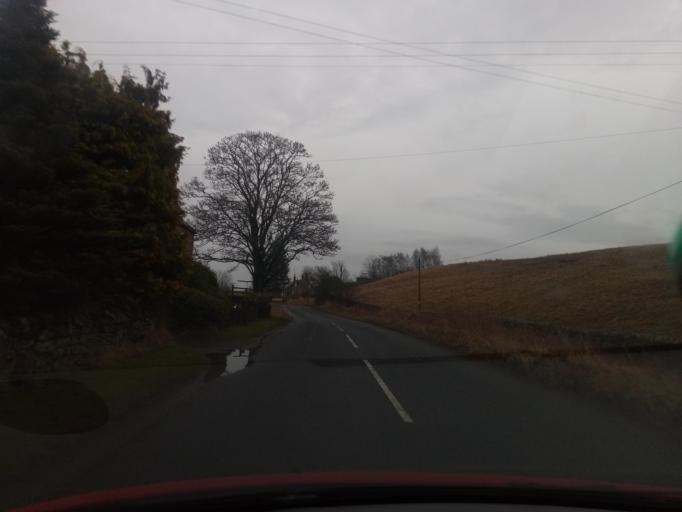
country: GB
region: England
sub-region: Northumberland
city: Rochester
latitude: 55.1658
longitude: -2.3719
